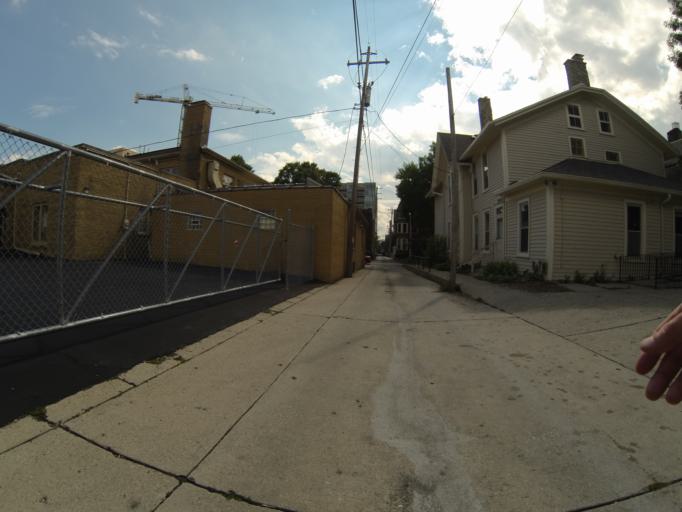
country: US
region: Wisconsin
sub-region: Milwaukee County
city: Milwaukee
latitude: 43.0558
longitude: -87.8904
